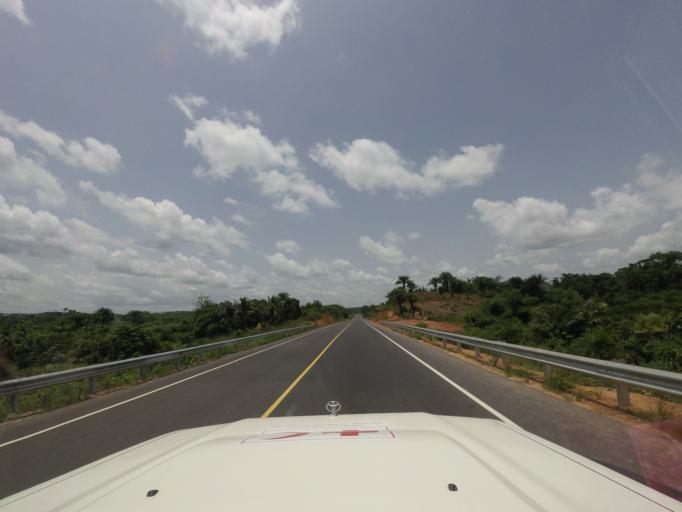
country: LR
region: Margibi
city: Kakata
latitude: 6.4369
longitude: -10.4587
